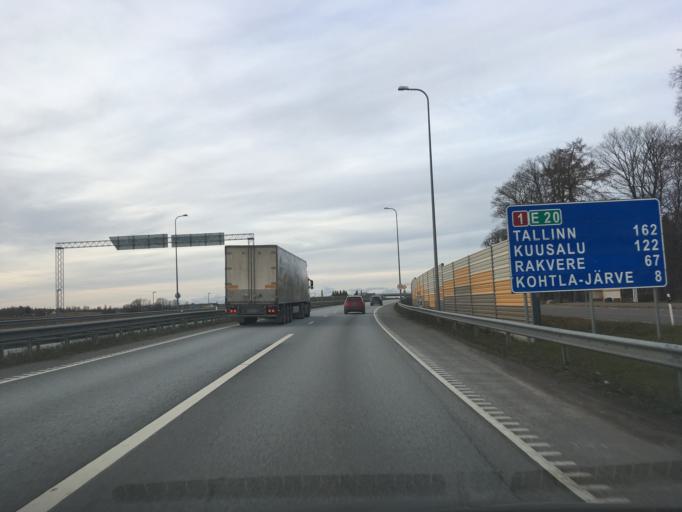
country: EE
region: Ida-Virumaa
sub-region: Johvi vald
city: Johvi
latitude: 59.3705
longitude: 27.3854
